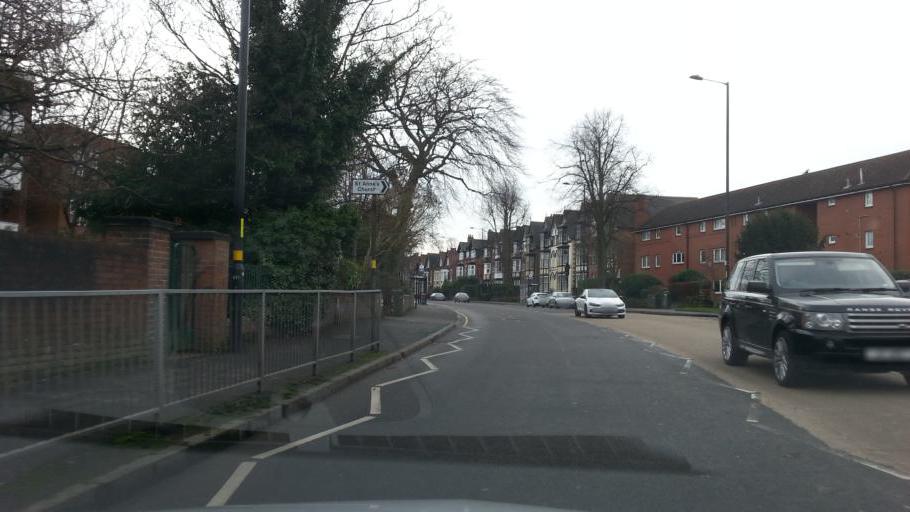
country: GB
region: England
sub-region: City and Borough of Birmingham
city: Birmingham
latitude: 52.4507
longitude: -1.8887
